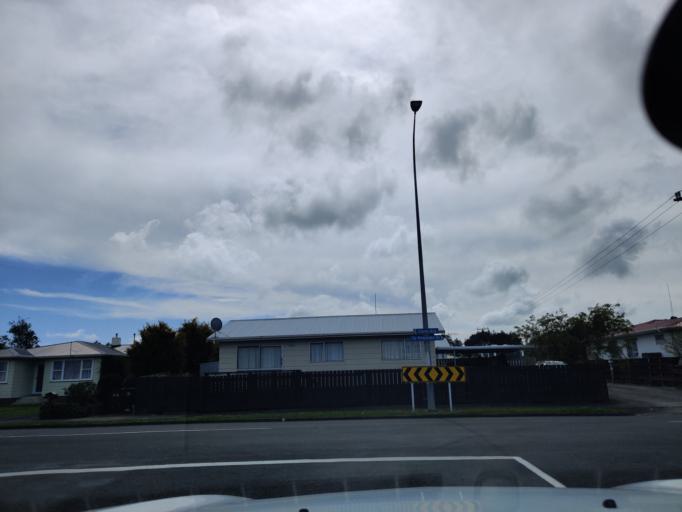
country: NZ
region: Manawatu-Wanganui
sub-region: Palmerston North City
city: Palmerston North
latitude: -40.3614
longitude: 175.5804
